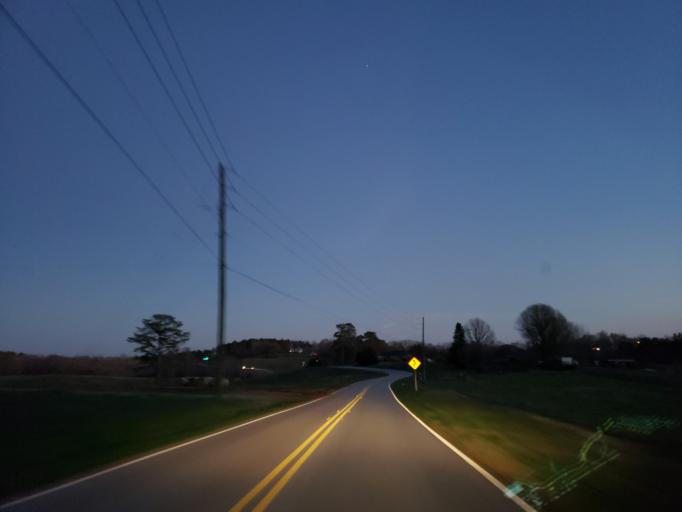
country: US
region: Georgia
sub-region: Bartow County
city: Emerson
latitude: 34.0662
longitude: -84.8141
